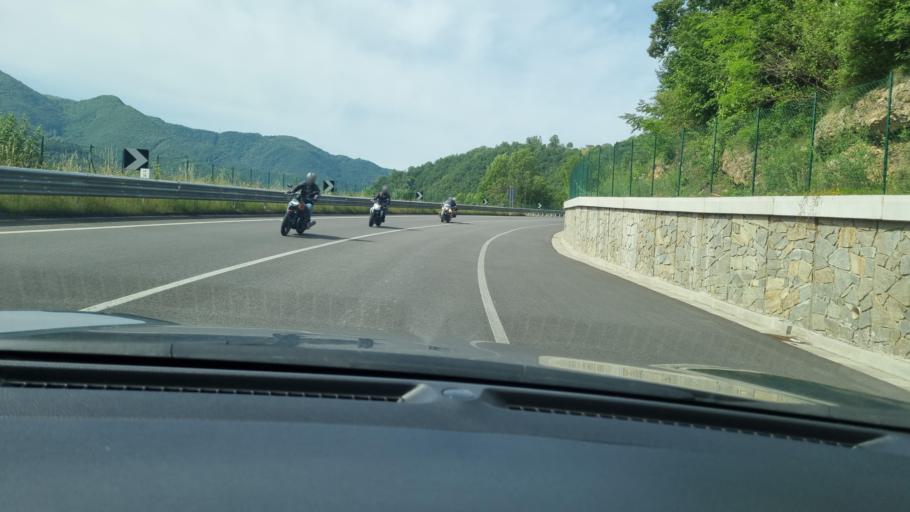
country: IT
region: Lombardy
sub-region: Provincia di Bergamo
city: Zogno
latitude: 45.8075
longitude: 9.6764
